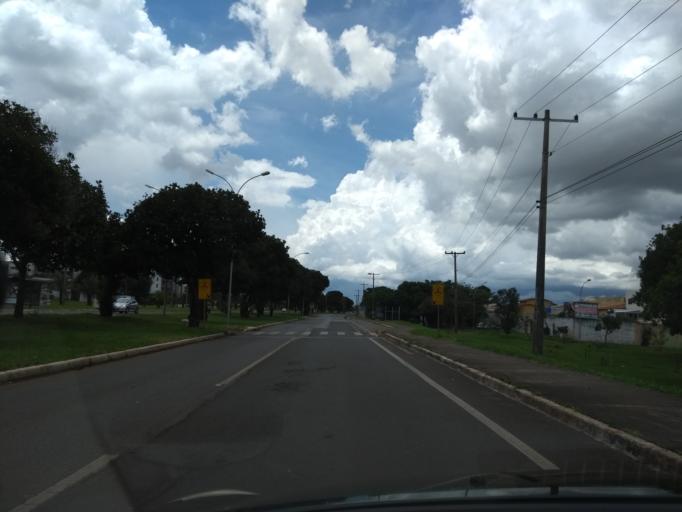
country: BR
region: Federal District
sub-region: Brasilia
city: Brasilia
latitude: -15.7866
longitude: -47.9315
